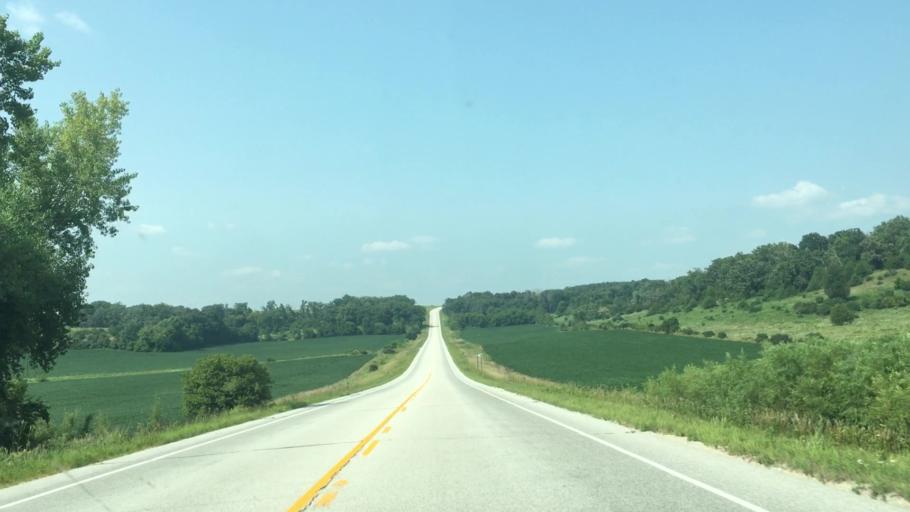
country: US
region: Minnesota
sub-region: Fillmore County
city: Harmony
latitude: 43.6308
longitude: -91.9299
